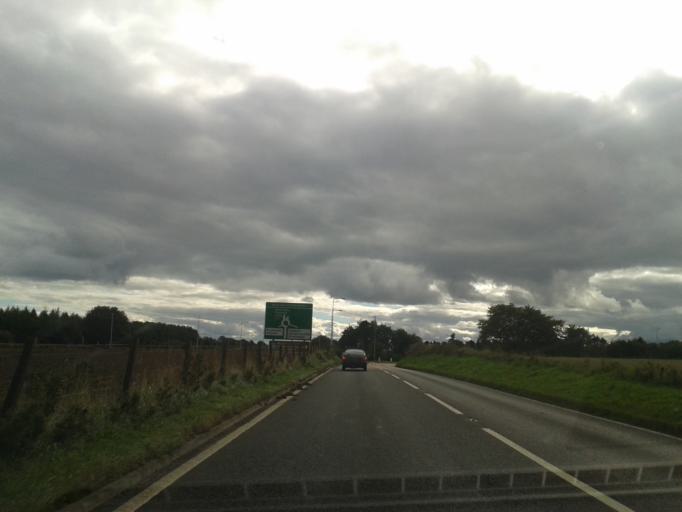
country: GB
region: Scotland
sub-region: Fife
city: Freuchie
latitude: 56.2355
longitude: -3.1551
